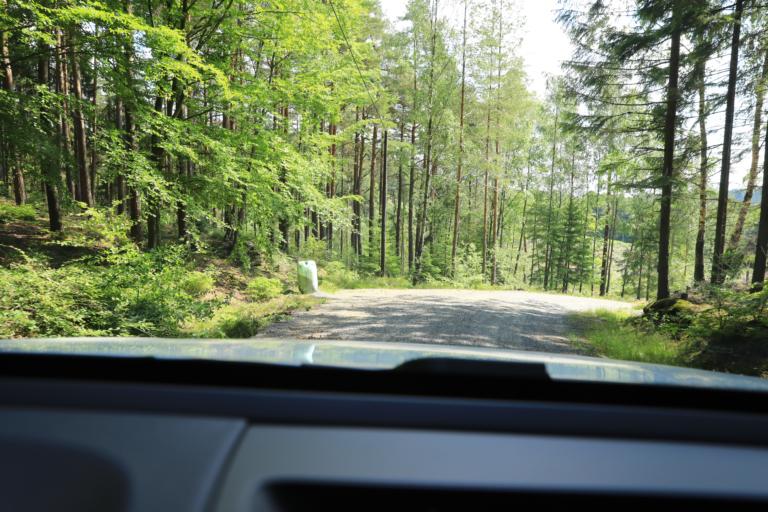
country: SE
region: Halland
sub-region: Varbergs Kommun
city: Veddige
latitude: 57.2135
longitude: 12.3495
